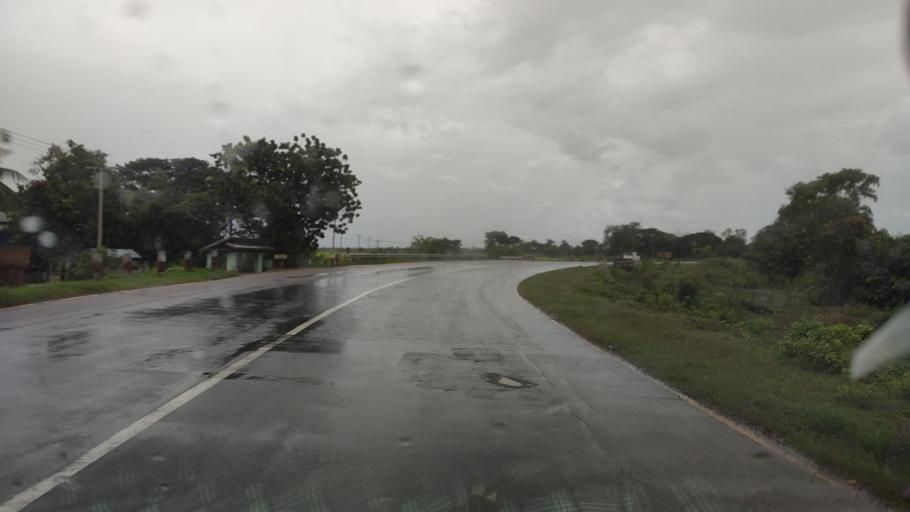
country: MM
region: Bago
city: Nyaunglebin
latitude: 17.7228
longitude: 96.6069
